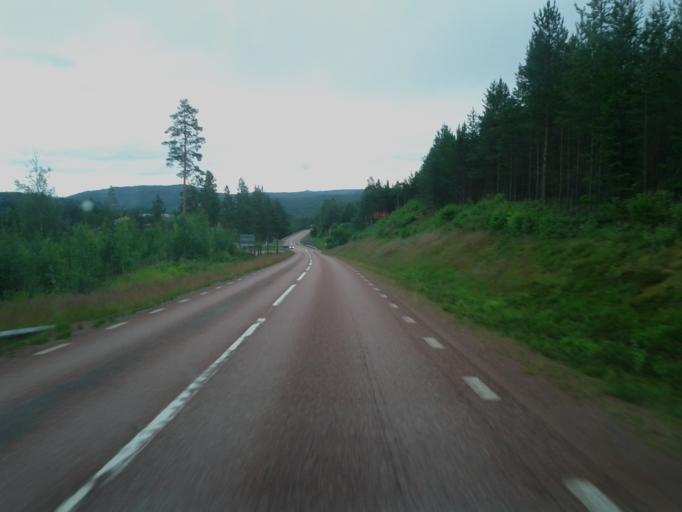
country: SE
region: Dalarna
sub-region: Alvdalens Kommun
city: AElvdalen
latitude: 61.2810
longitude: 13.7619
